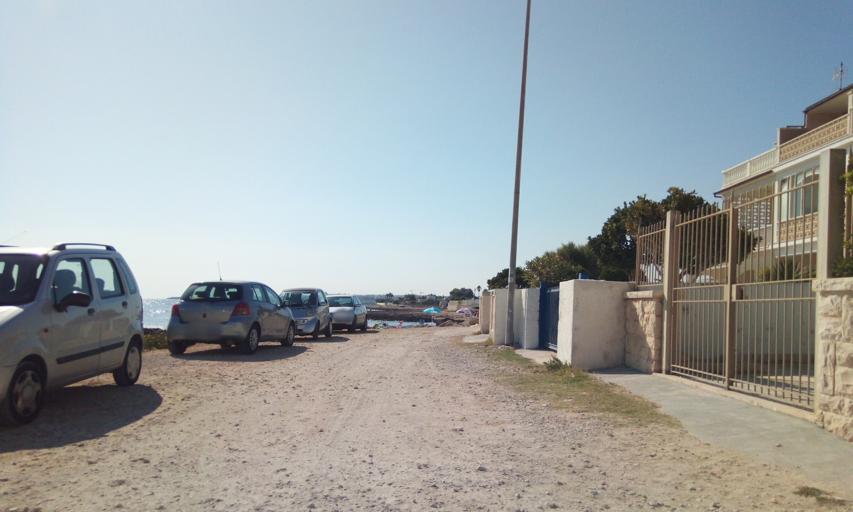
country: IT
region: Apulia
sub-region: Provincia di Bari
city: Polignano a Mare
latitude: 41.0138
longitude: 17.1948
